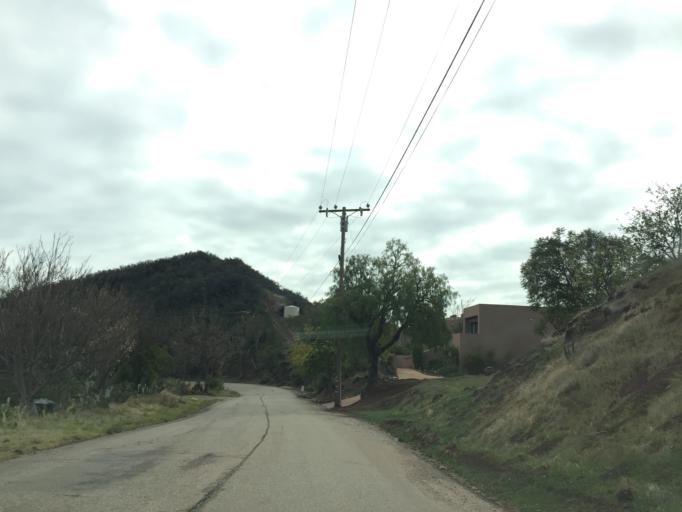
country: US
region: California
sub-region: Santa Barbara County
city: Goleta
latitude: 34.4807
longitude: -119.7977
